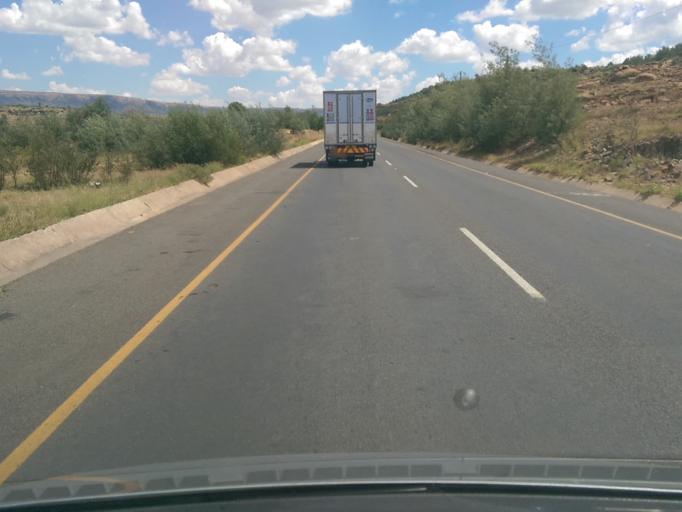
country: LS
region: Maseru
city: Maseru
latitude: -29.3945
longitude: 27.5404
